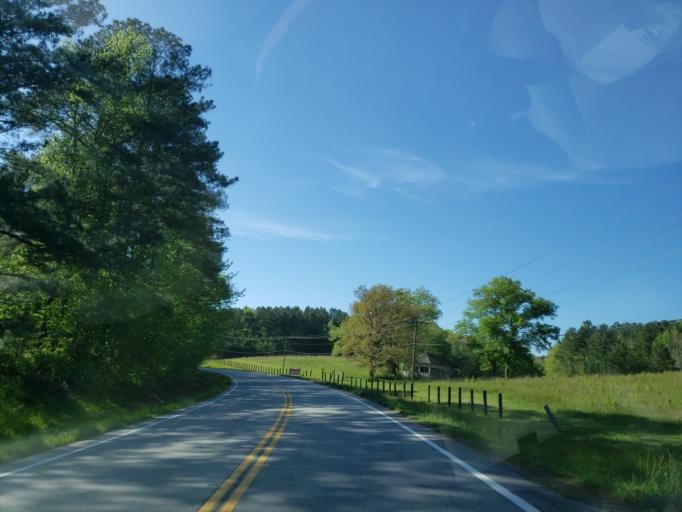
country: US
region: Georgia
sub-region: Haralson County
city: Tallapoosa
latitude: 33.8748
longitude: -85.3019
